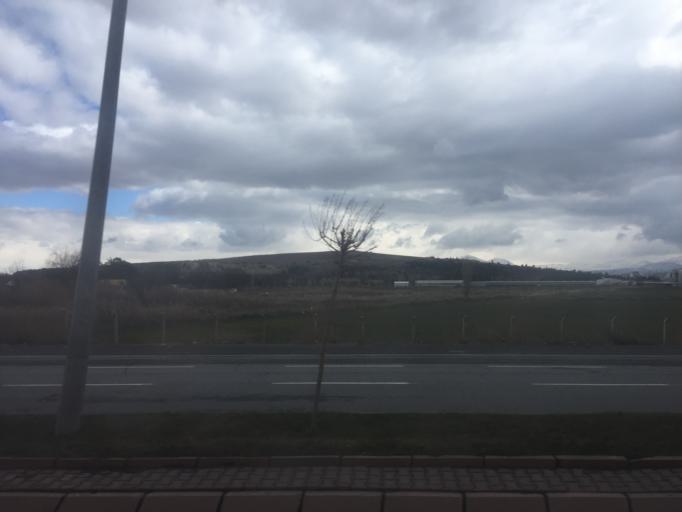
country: TR
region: Kayseri
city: Melikgazi
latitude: 38.7581
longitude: 35.4107
